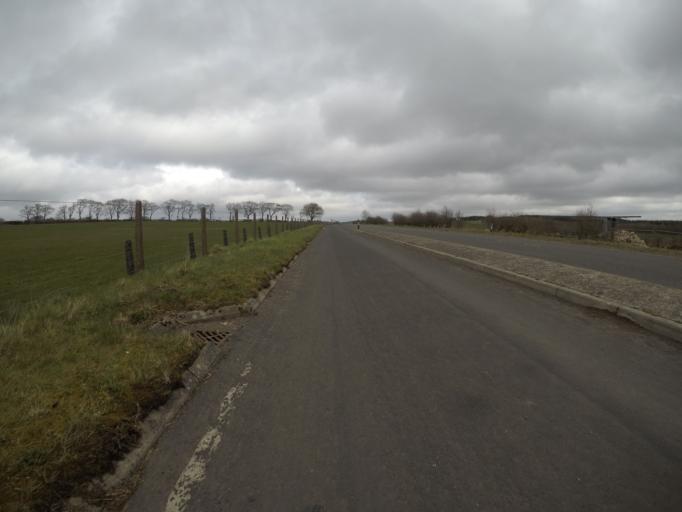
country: GB
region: Scotland
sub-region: East Ayrshire
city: Stewarton
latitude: 55.6751
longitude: -4.4352
